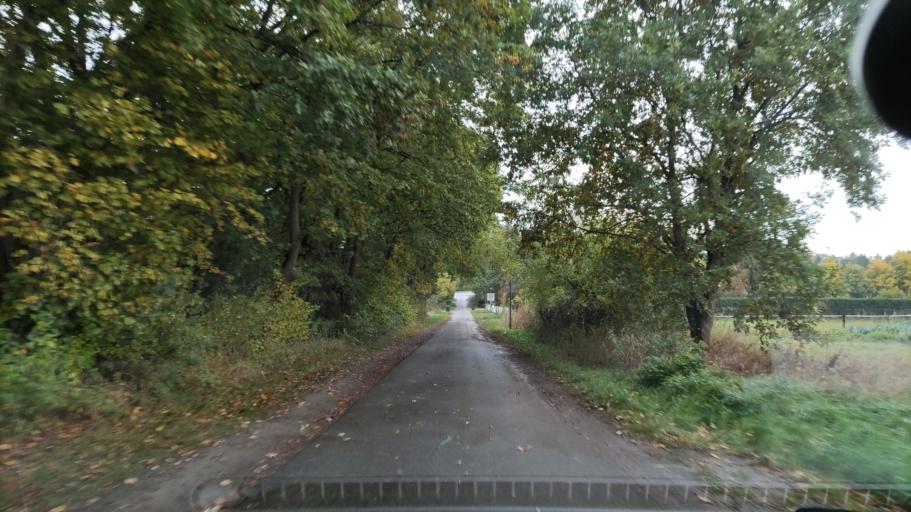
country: DE
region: Lower Saxony
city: Deutsch Evern
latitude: 53.1965
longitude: 10.4438
